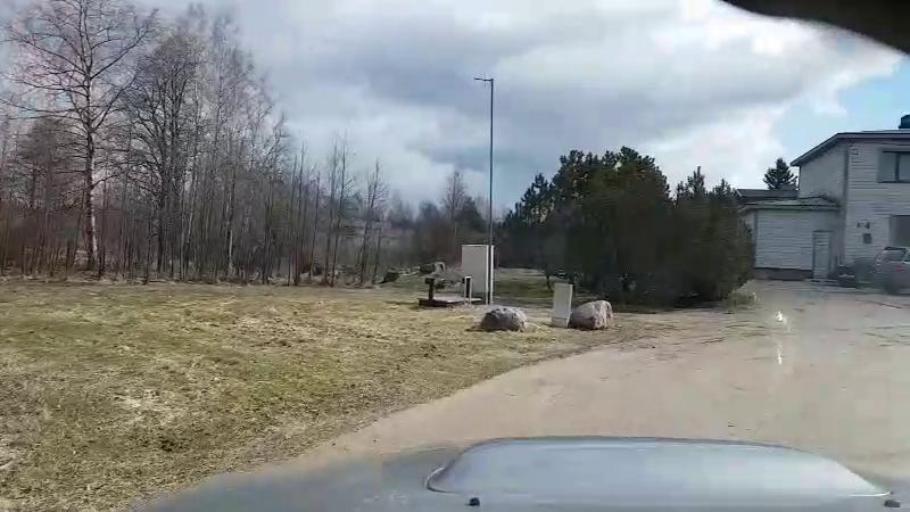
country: EE
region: Jaervamaa
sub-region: Paide linn
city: Paide
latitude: 58.8871
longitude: 25.5772
